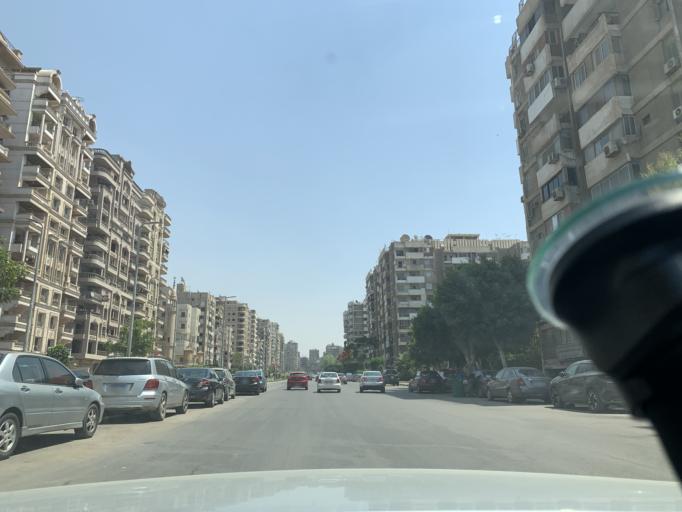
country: EG
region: Muhafazat al Qahirah
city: Cairo
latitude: 30.0680
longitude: 31.3487
